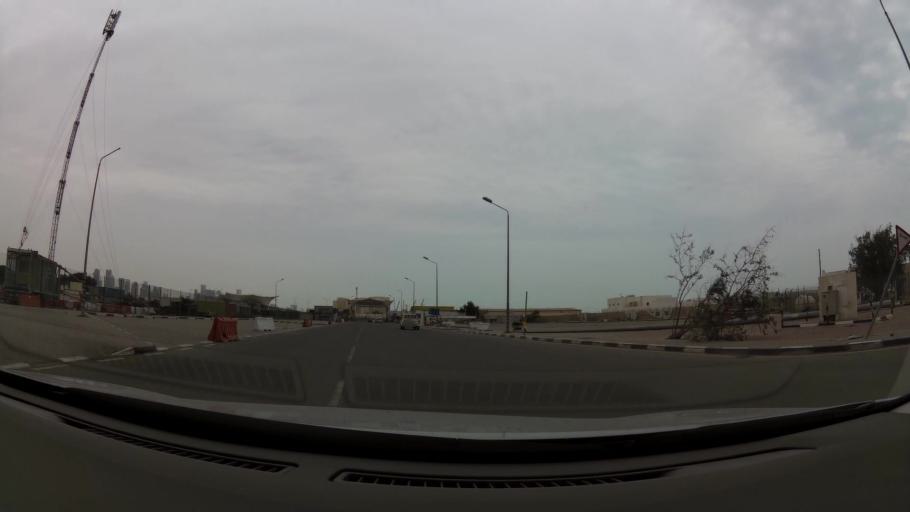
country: QA
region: Baladiyat ad Dawhah
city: Doha
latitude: 25.2929
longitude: 51.5467
